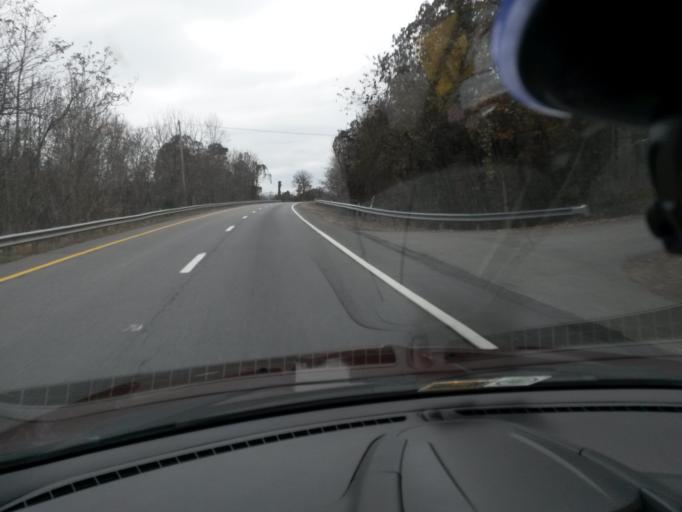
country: US
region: Virginia
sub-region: Nelson County
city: Nellysford
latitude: 37.8430
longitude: -78.7843
